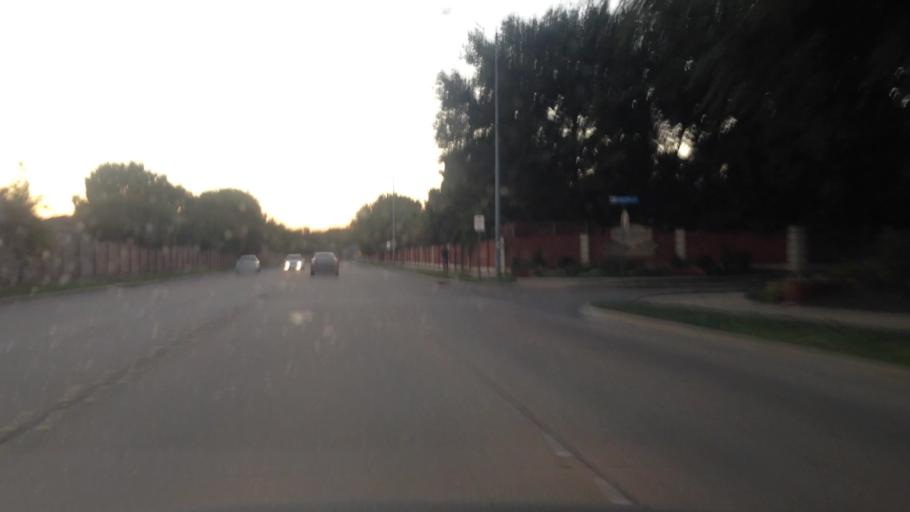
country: US
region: Texas
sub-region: Tarrant County
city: Watauga
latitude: 32.8546
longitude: -97.2778
